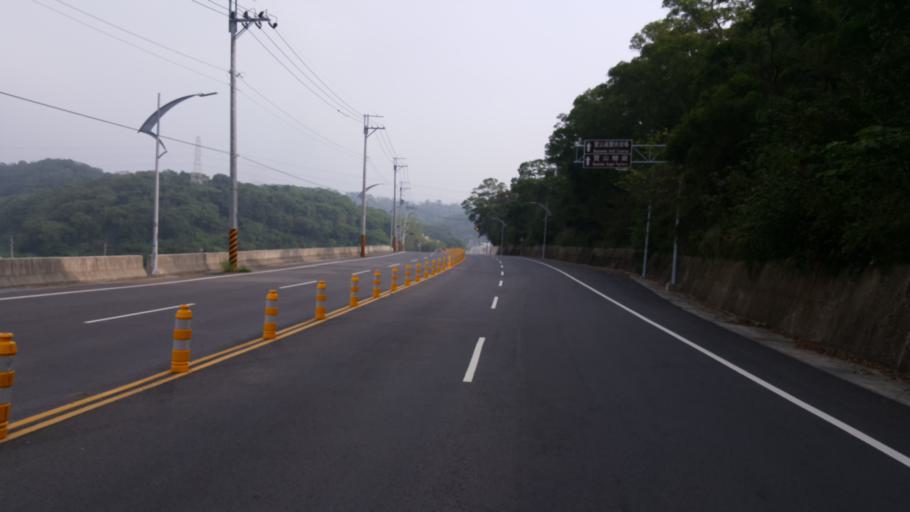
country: TW
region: Taiwan
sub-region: Hsinchu
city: Hsinchu
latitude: 24.7438
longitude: 120.9590
